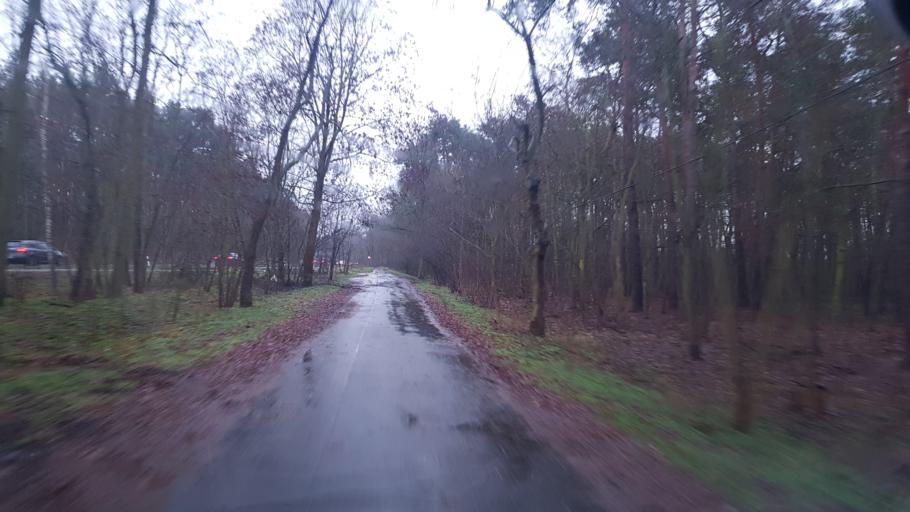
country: DE
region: Brandenburg
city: Ludwigsfelde
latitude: 52.3076
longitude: 13.2055
